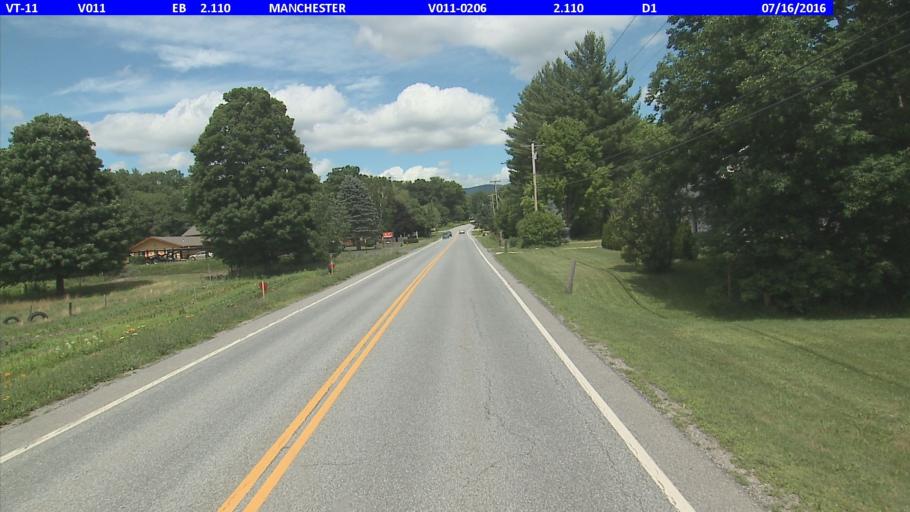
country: US
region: Vermont
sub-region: Bennington County
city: Manchester Center
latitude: 43.1760
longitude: -73.0189
